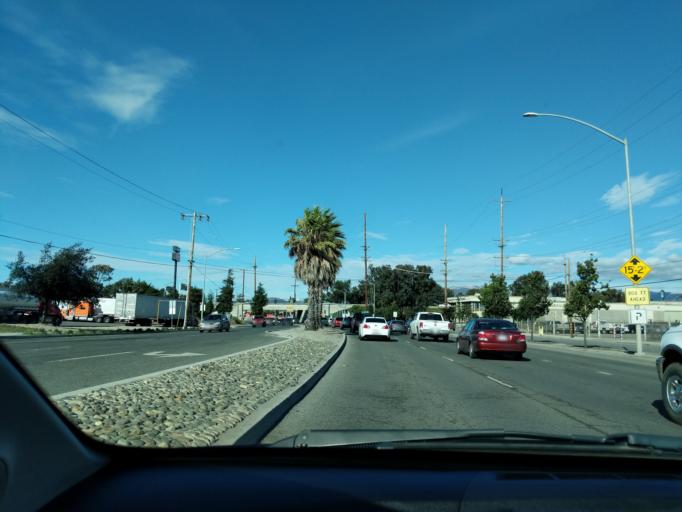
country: US
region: California
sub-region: Monterey County
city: Salinas
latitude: 36.6649
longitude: -121.6292
